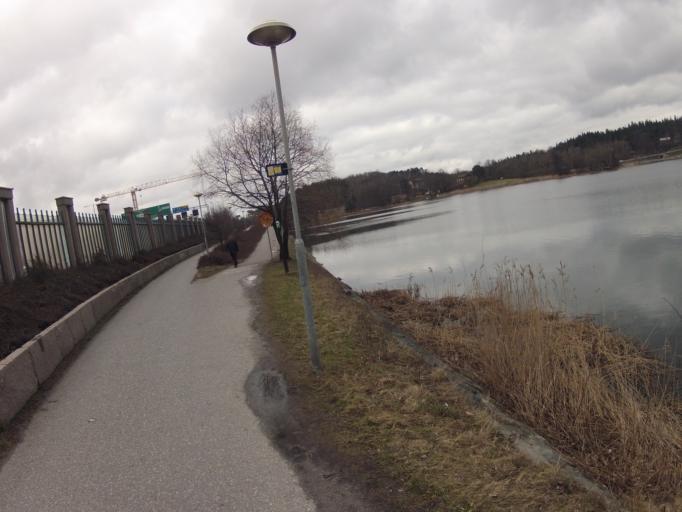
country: SE
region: Stockholm
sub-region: Norrtalje Kommun
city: Bergshamra
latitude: 59.3753
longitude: 18.0168
